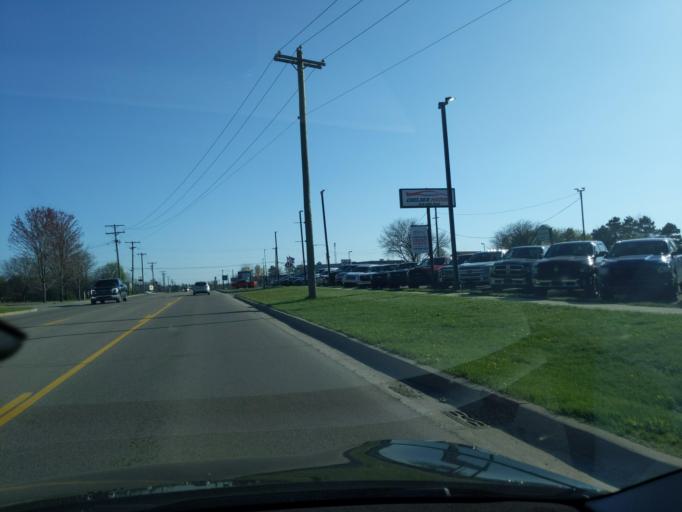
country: US
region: Michigan
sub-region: Washtenaw County
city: Chelsea
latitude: 42.3011
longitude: -84.0236
